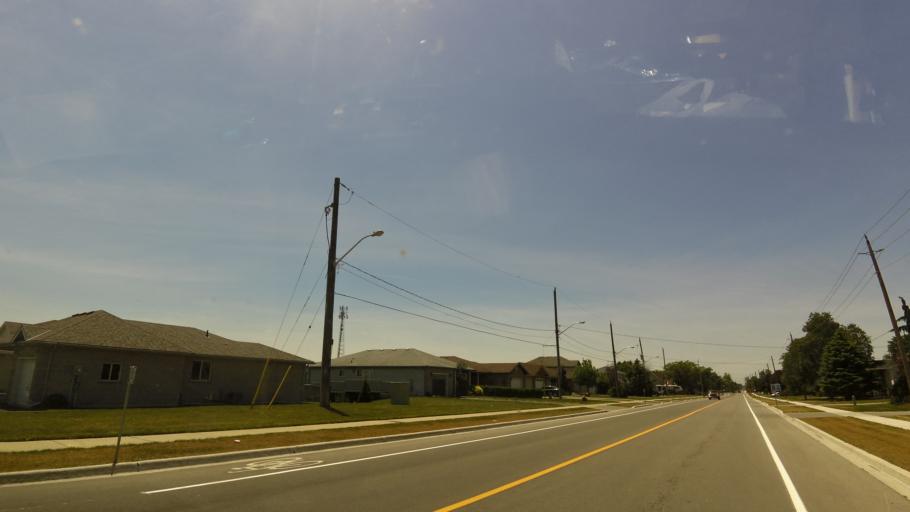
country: CA
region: Ontario
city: Ingersoll
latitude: 42.8820
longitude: -80.7221
